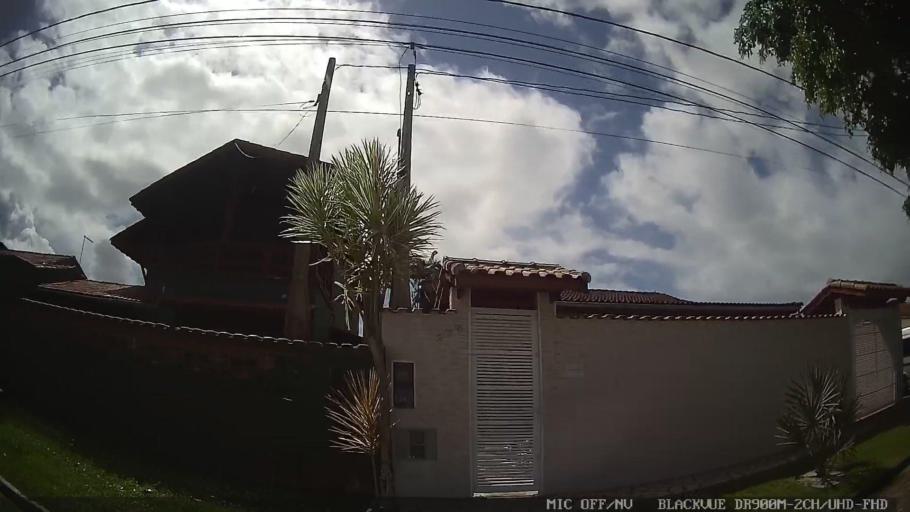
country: BR
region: Sao Paulo
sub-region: Itanhaem
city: Itanhaem
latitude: -24.2269
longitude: -46.8662
